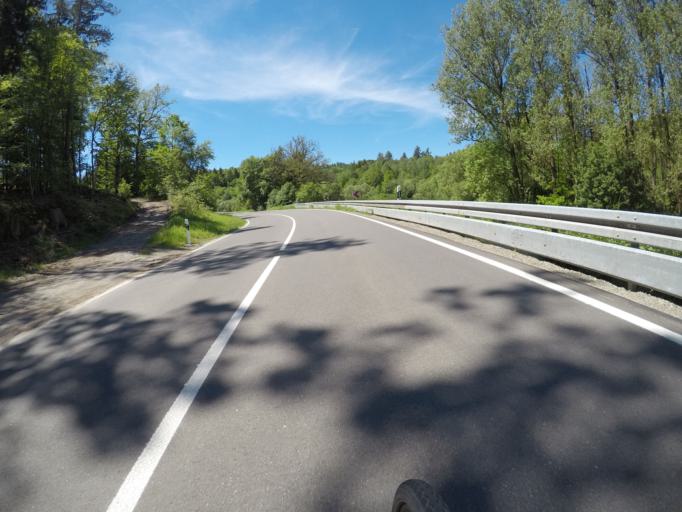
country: DE
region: Baden-Wuerttemberg
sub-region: Karlsruhe Region
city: Neuhausen
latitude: 48.8086
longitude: 8.8054
